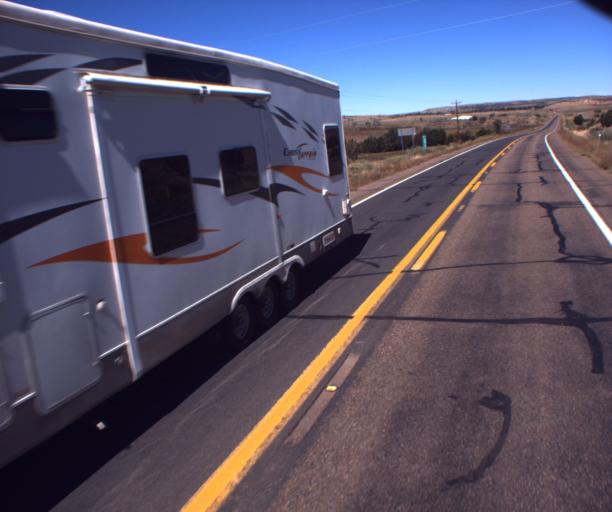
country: US
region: Arizona
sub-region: Apache County
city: Saint Johns
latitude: 34.4042
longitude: -109.4107
